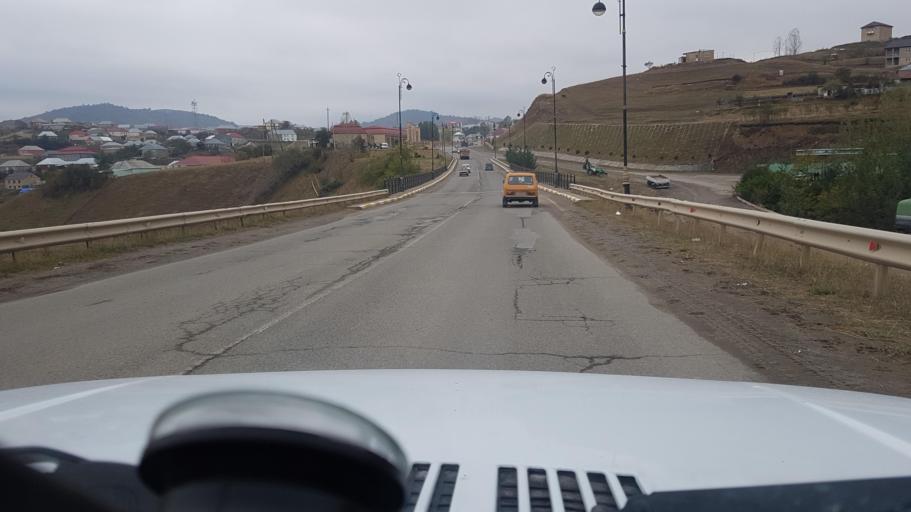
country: AZ
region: Gadabay Rayon
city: Ariqdam
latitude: 40.5869
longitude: 45.8109
